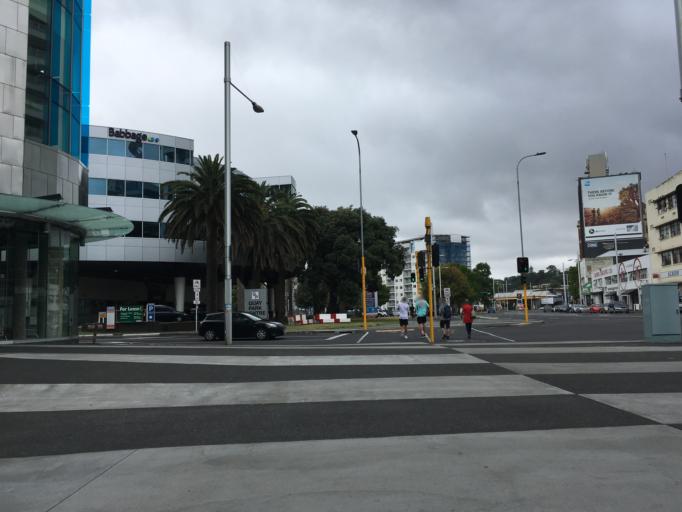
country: NZ
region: Auckland
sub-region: Auckland
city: Auckland
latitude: -36.8472
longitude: 174.7737
